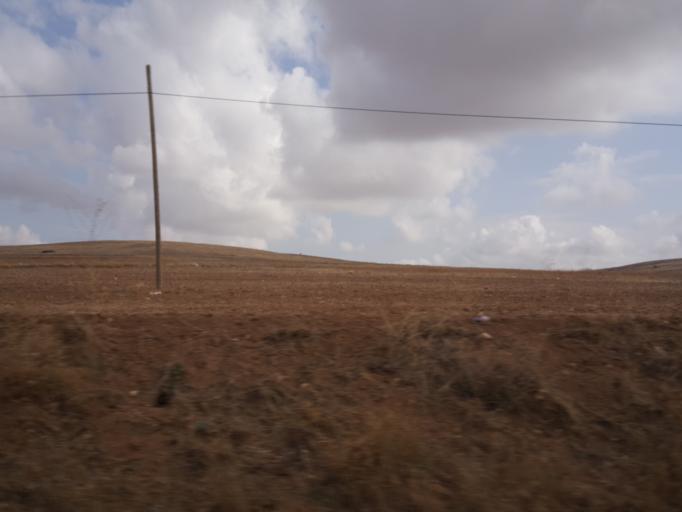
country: TR
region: Kirikkale
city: Keskin
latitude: 39.6344
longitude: 33.6086
